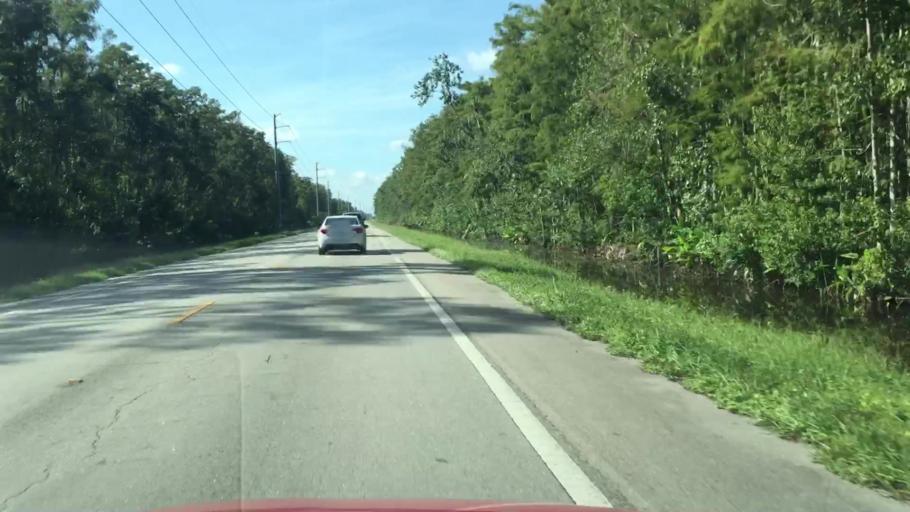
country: US
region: Florida
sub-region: Collier County
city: Orangetree
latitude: 26.3429
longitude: -81.5952
